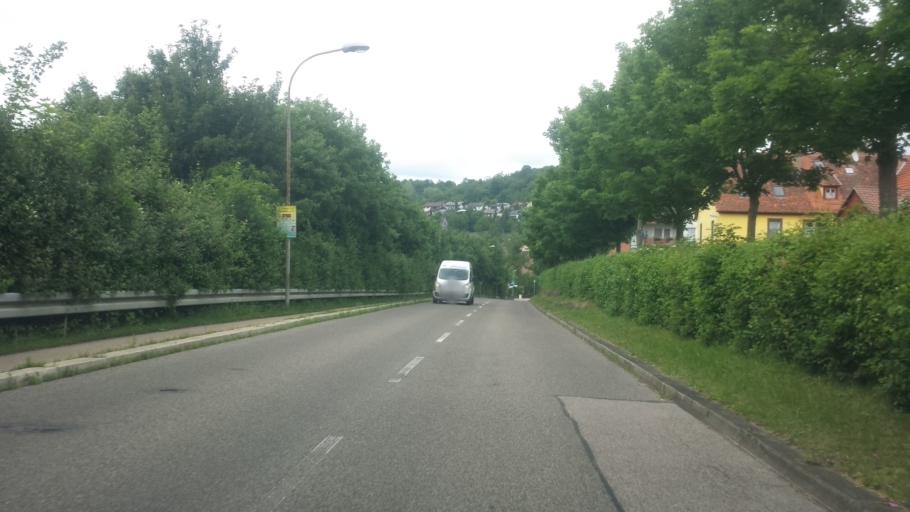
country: DE
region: Baden-Wuerttemberg
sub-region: Regierungsbezirk Stuttgart
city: Creglingen
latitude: 49.4671
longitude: 10.0307
